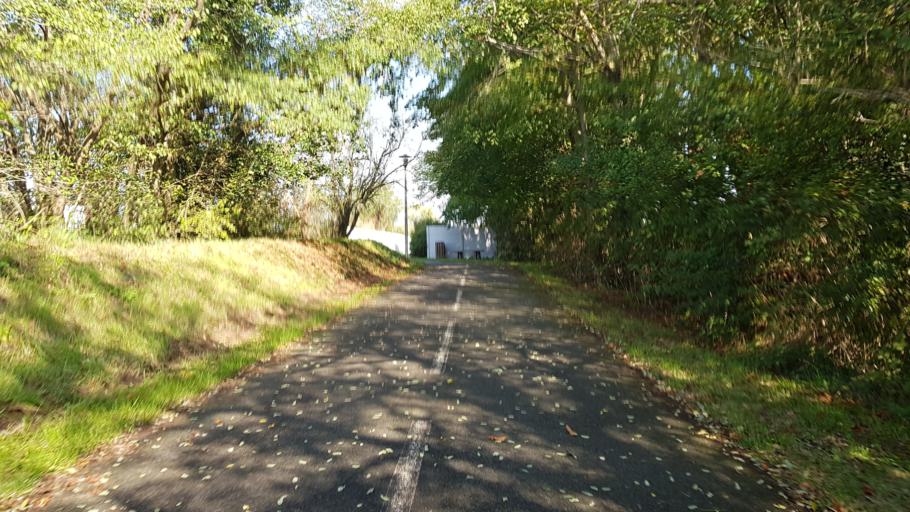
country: FR
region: Poitou-Charentes
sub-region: Departement de la Vienne
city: Chasseneuil-du-Poitou
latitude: 46.6544
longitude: 0.3752
